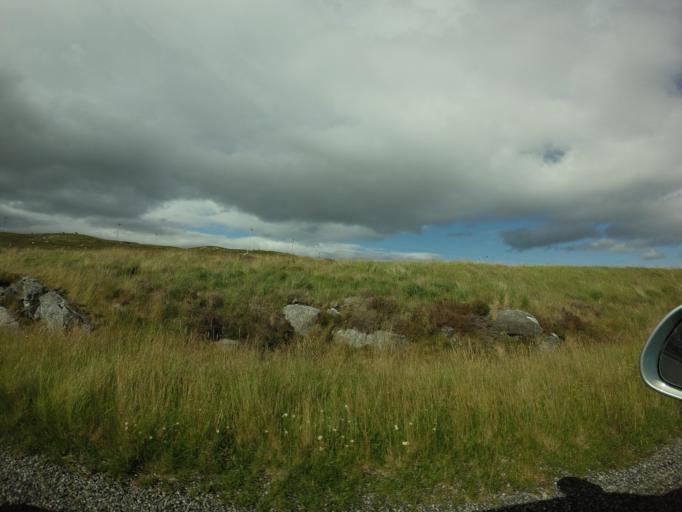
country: GB
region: Scotland
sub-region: Eilean Siar
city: Harris
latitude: 58.1964
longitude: -6.7200
